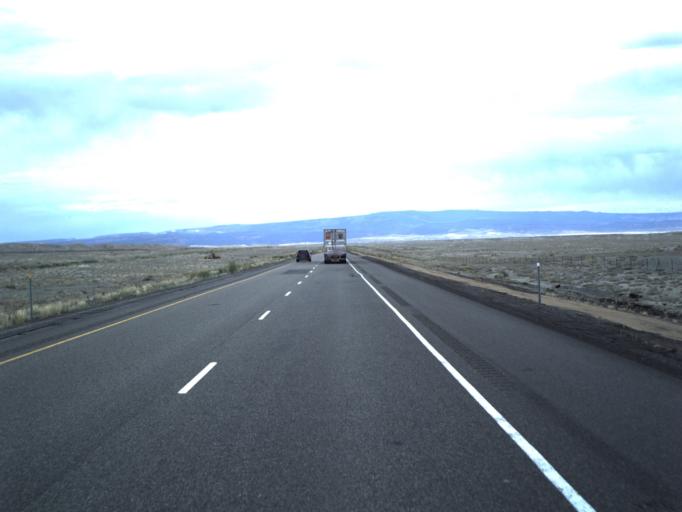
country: US
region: Utah
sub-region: Grand County
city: Moab
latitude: 38.9355
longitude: -109.4701
